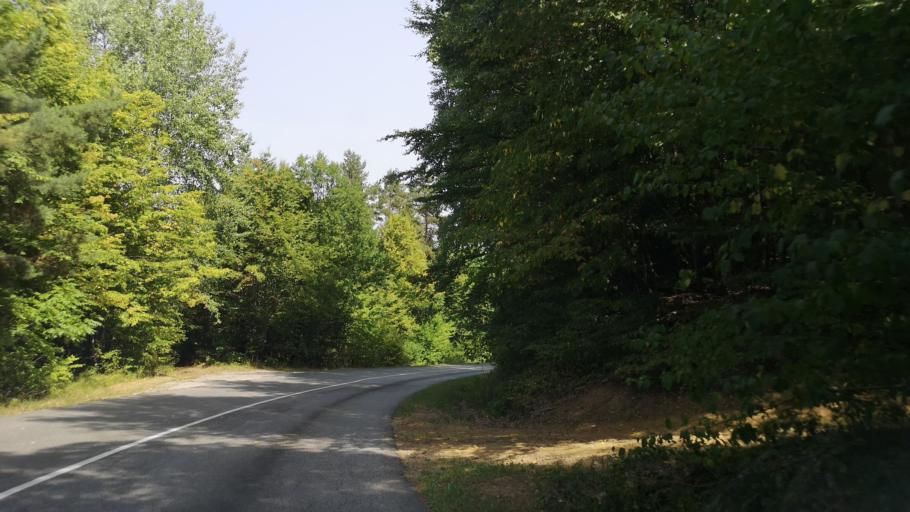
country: SK
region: Kosicky
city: Dobsina
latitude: 48.7199
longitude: 20.3967
